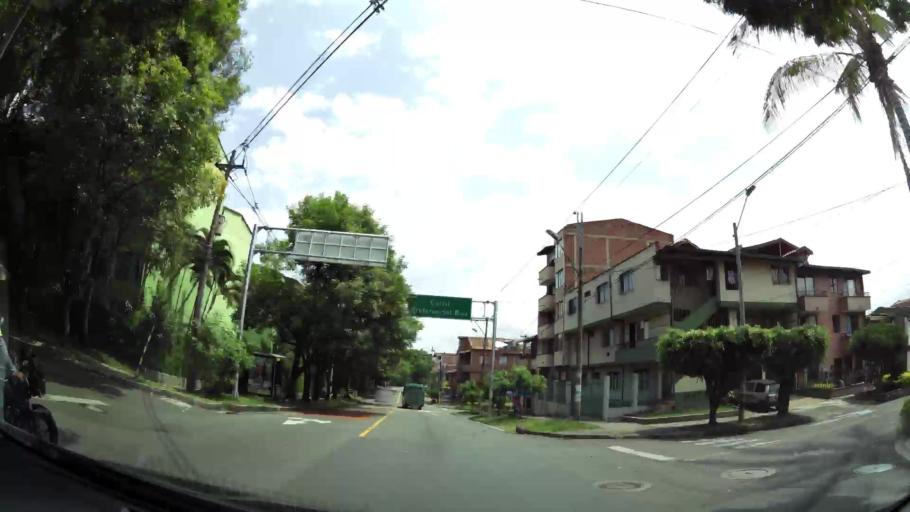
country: CO
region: Antioquia
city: Medellin
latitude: 6.2511
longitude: -75.6112
